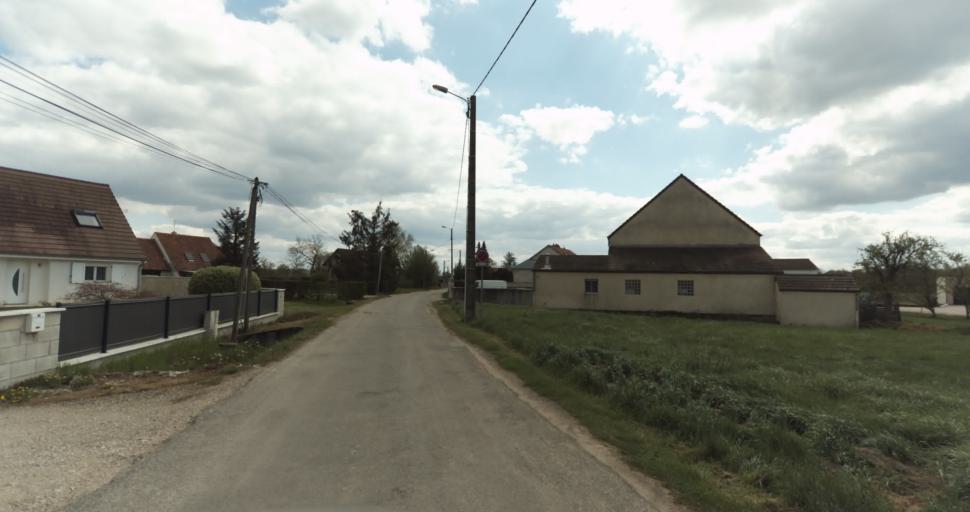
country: FR
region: Bourgogne
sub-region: Departement de la Cote-d'Or
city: Auxonne
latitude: 47.1812
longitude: 5.3922
